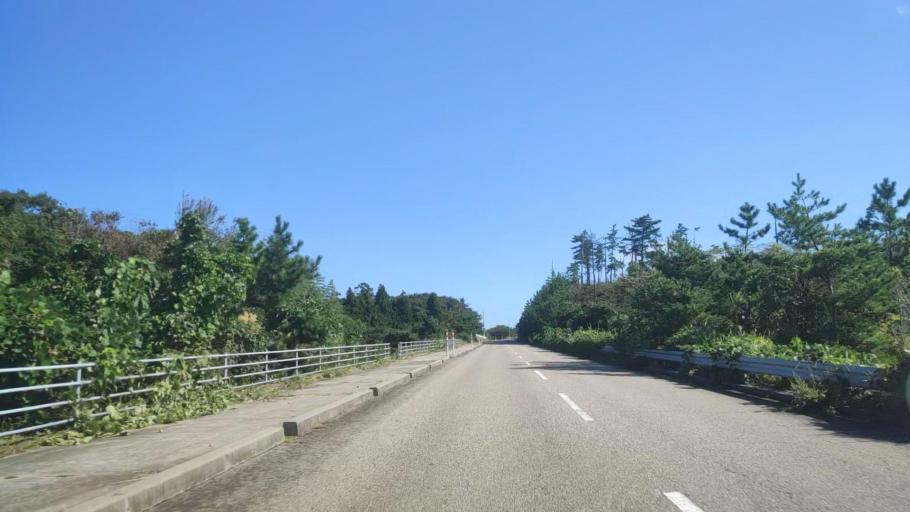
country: JP
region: Ishikawa
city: Hakui
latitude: 37.0750
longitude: 136.7226
